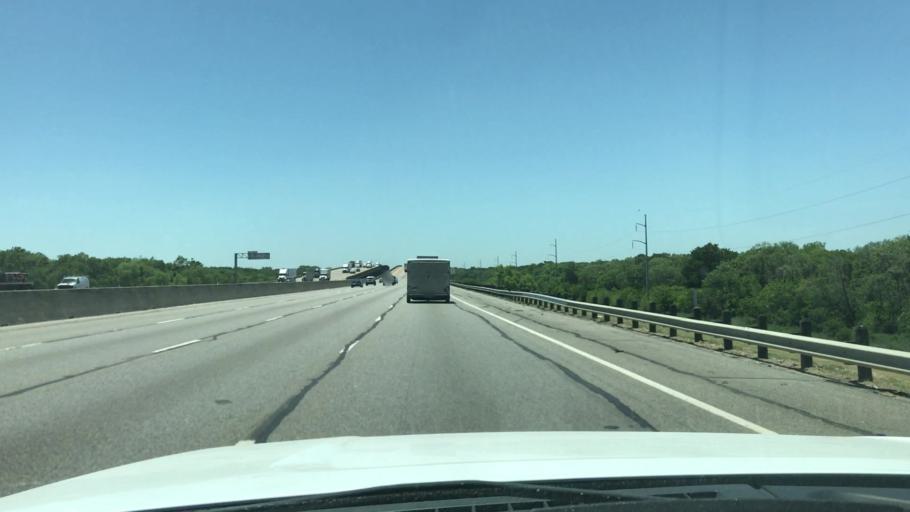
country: US
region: Texas
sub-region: Dallas County
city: Hutchins
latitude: 32.6785
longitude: -96.6823
